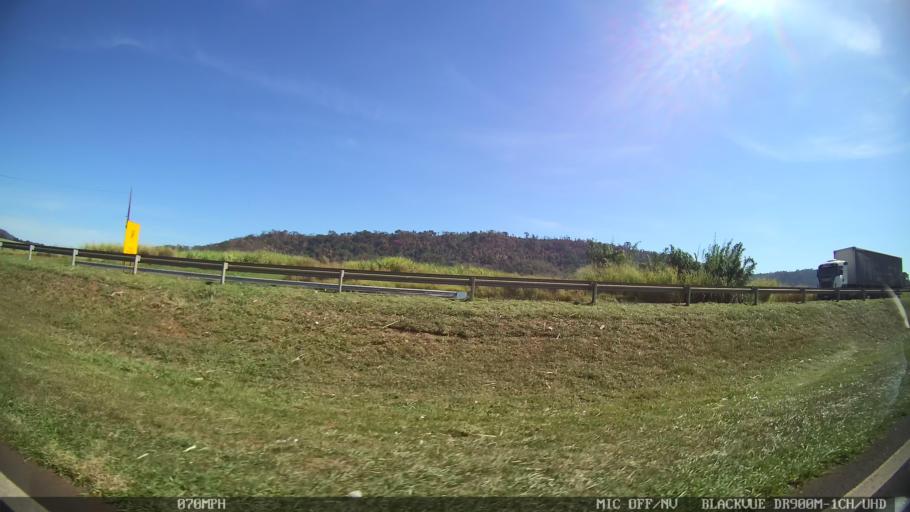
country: BR
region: Sao Paulo
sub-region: Sao Simao
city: Sao Simao
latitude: -21.5216
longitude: -47.6432
